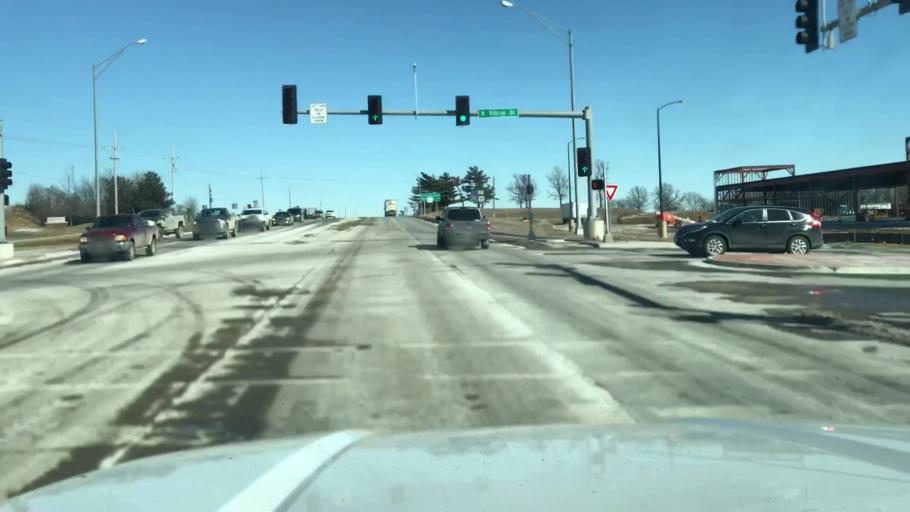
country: US
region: Missouri
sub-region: Andrew County
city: Country Club Village
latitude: 39.8120
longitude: -94.8065
